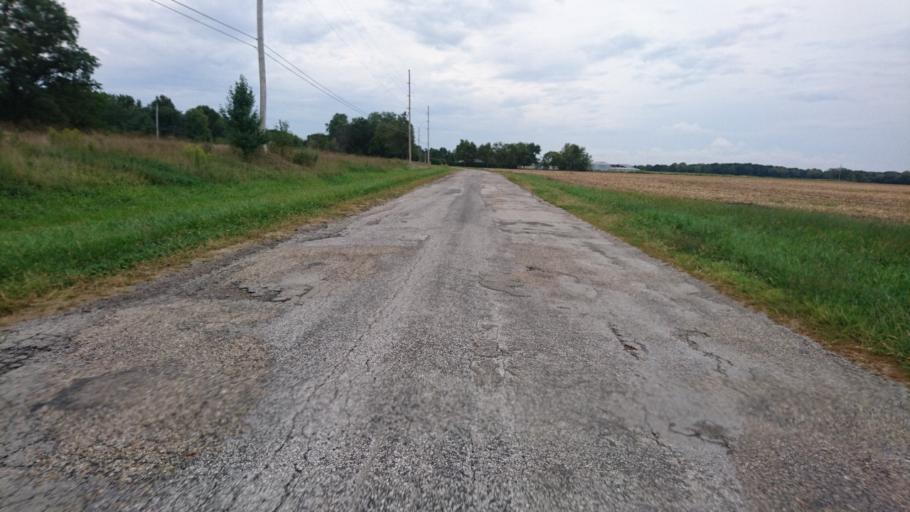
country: US
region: Illinois
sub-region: Sangamon County
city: Southern View
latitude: 39.7196
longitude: -89.6806
